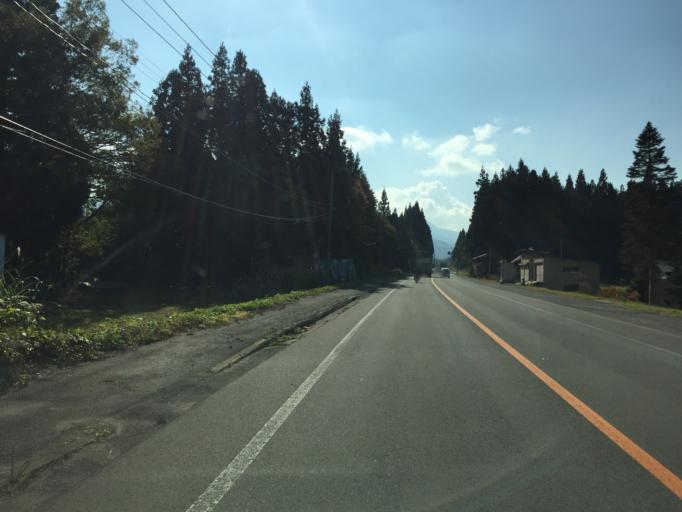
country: JP
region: Yamagata
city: Yonezawa
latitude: 37.8953
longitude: 140.0155
